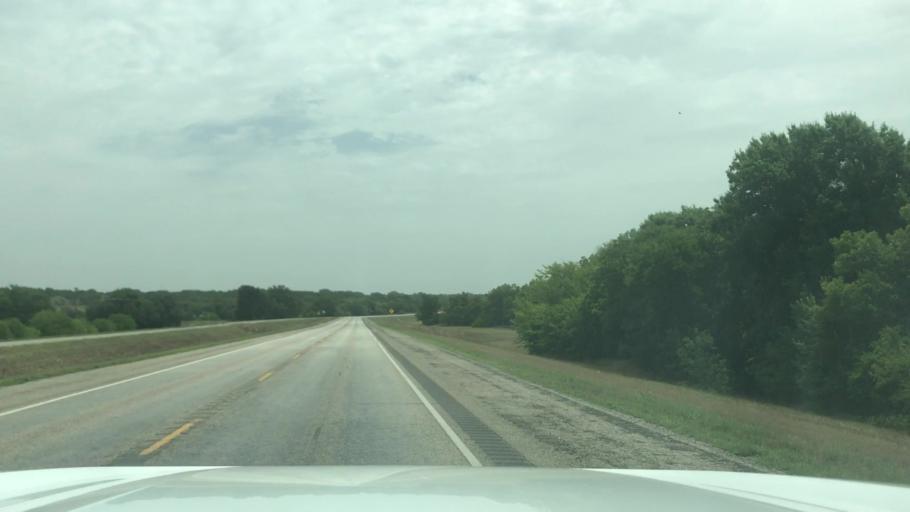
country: US
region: Texas
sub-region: Hamilton County
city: Hico
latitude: 32.0393
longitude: -98.1061
